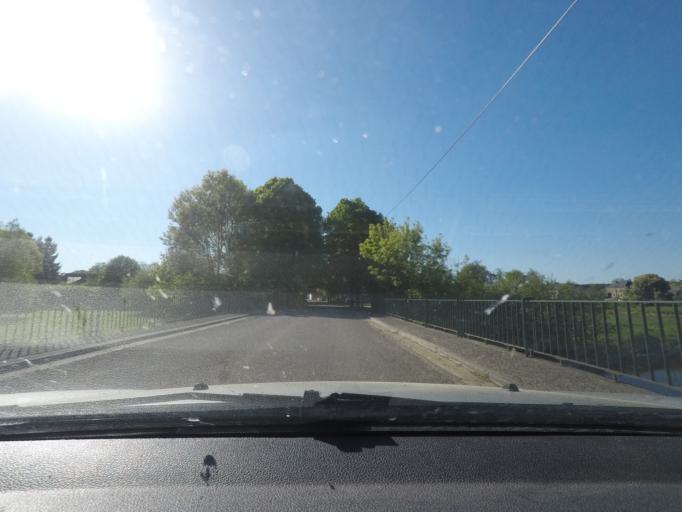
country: BE
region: Wallonia
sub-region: Province du Luxembourg
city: Tintigny
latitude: 49.7058
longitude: 5.4600
